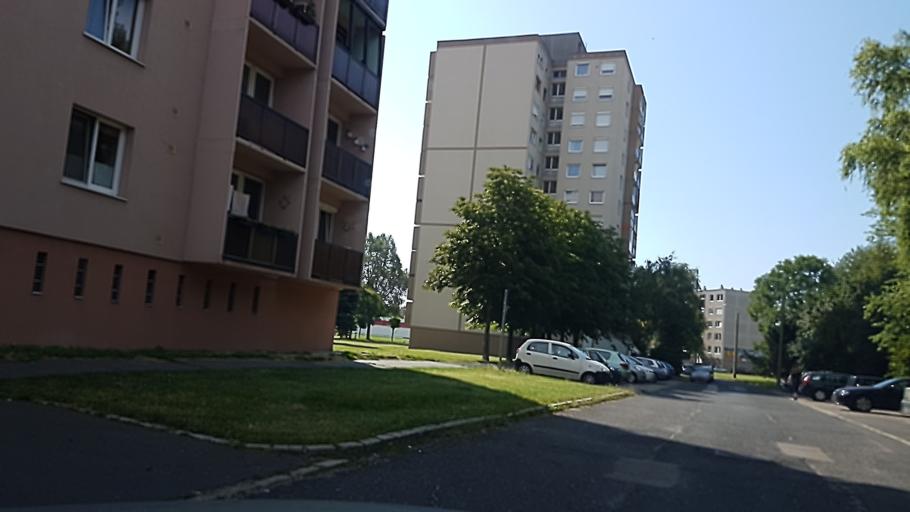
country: HU
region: Gyor-Moson-Sopron
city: Sopron
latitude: 47.6924
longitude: 16.5738
